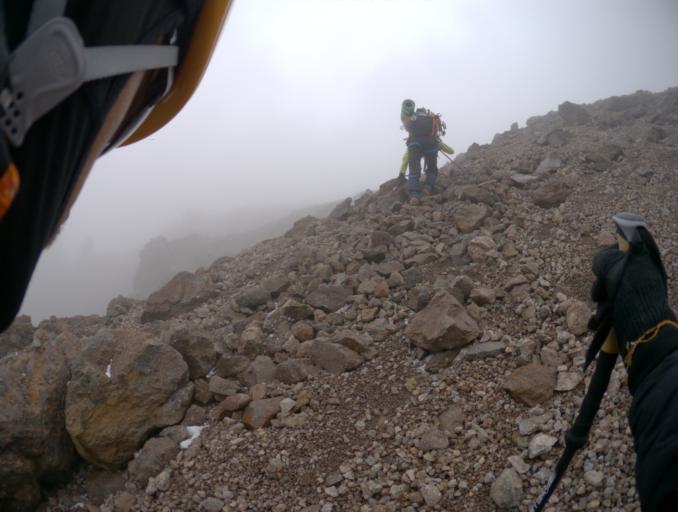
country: RU
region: Kabardino-Balkariya
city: Terskol
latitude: 43.3797
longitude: 42.4077
